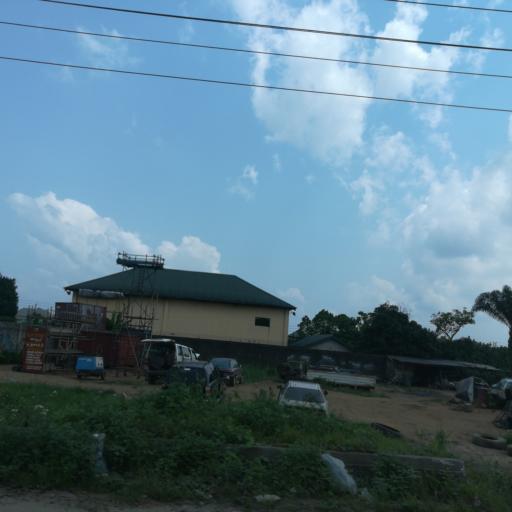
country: NG
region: Rivers
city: Port Harcourt
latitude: 4.8458
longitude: 7.0765
